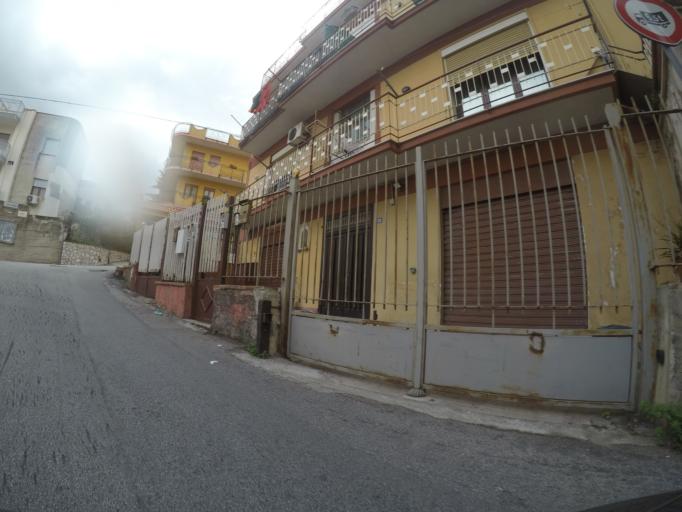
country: IT
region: Sicily
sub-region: Palermo
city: Carini
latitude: 38.1287
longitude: 13.1816
